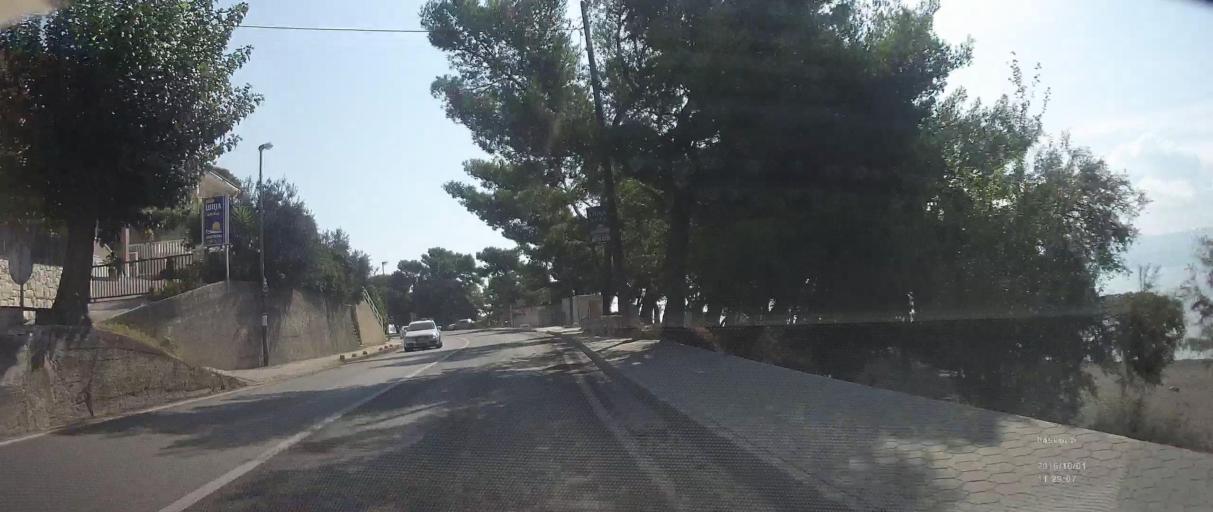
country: HR
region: Splitsko-Dalmatinska
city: Duce
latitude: 43.4400
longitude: 16.6634
